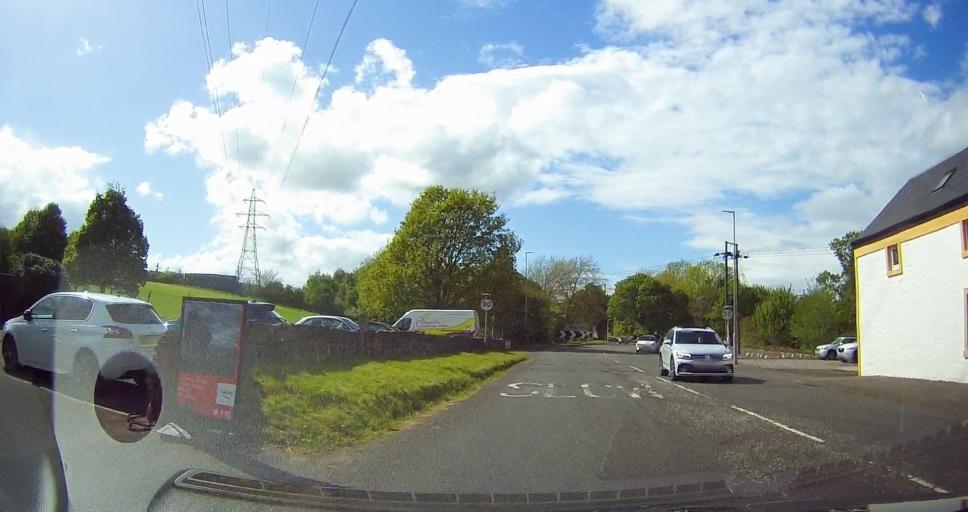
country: GB
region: Scotland
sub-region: Falkirk
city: Larbert
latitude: 56.0147
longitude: -3.8291
